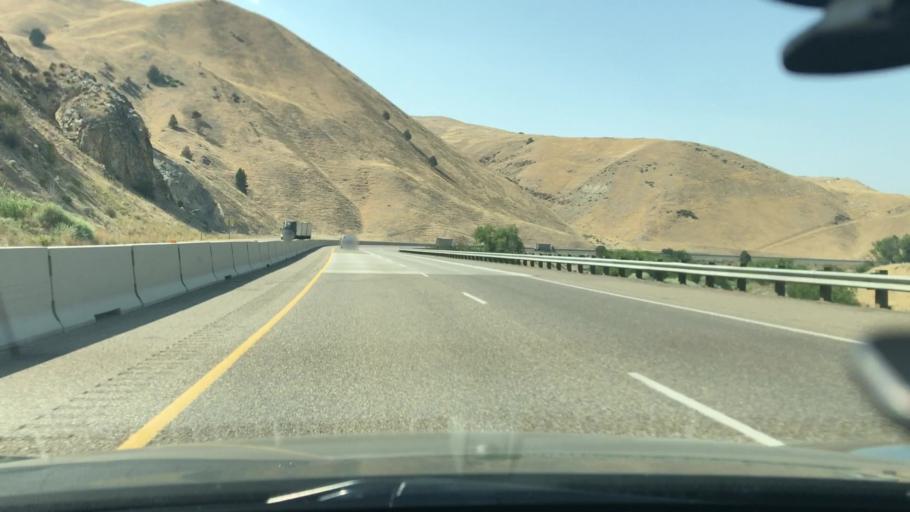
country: US
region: Idaho
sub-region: Washington County
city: Weiser
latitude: 44.4029
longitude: -117.3100
